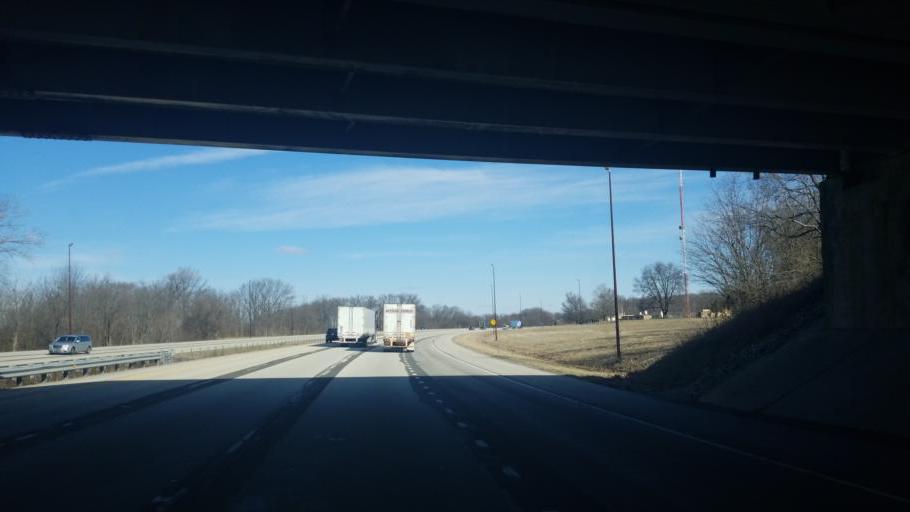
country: US
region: Illinois
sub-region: Sangamon County
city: Chatham
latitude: 39.6866
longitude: -89.6430
